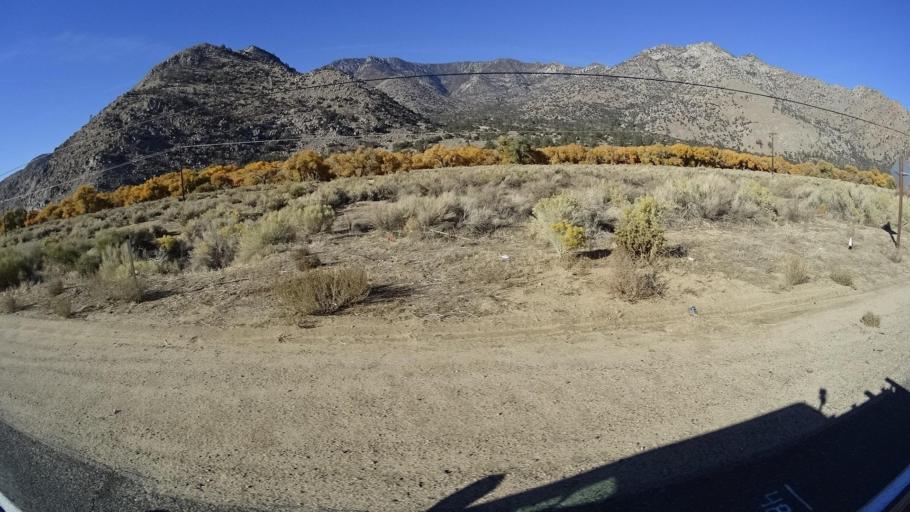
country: US
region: California
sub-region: Kern County
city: Weldon
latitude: 35.6937
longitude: -118.2214
